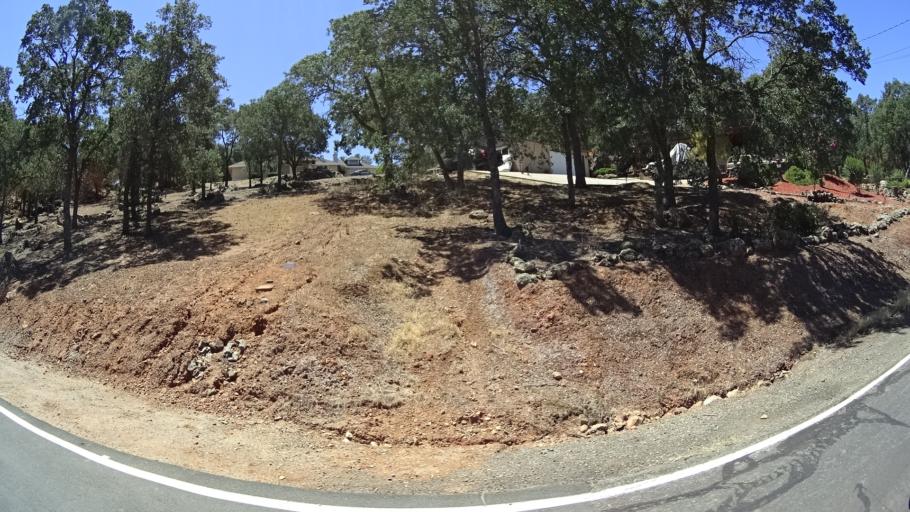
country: US
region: California
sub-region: Calaveras County
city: Rancho Calaveras
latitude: 38.1420
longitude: -120.8394
